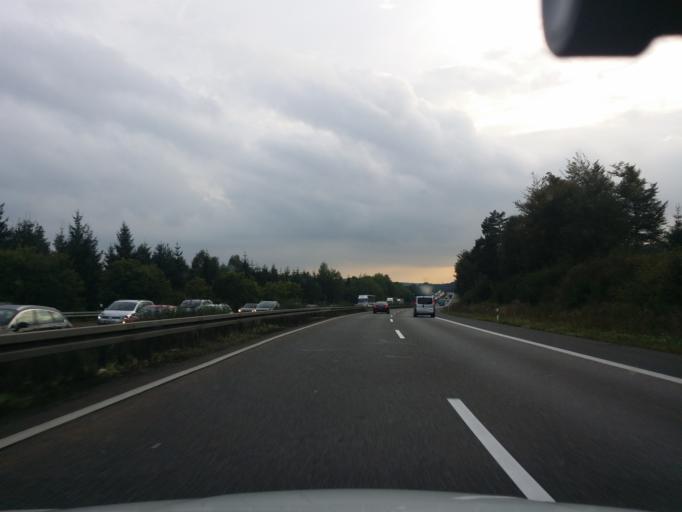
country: DE
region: Hesse
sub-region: Regierungsbezirk Kassel
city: Ottrau
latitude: 50.7753
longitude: 9.3941
